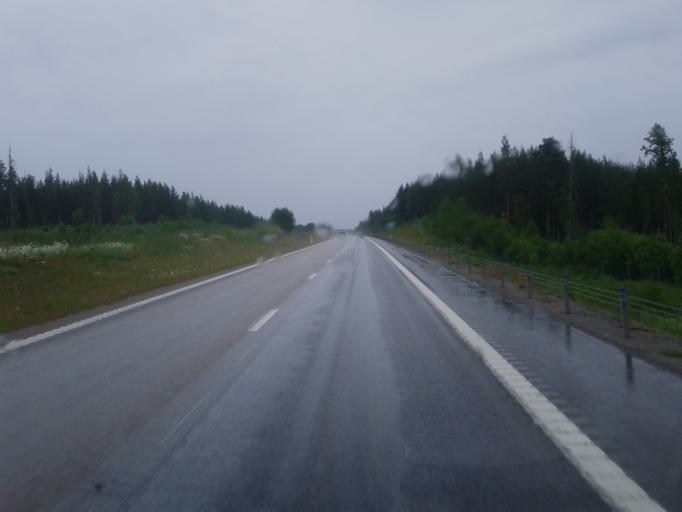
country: SE
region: Uppsala
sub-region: Tierps Kommun
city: Tierp
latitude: 60.2414
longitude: 17.5021
